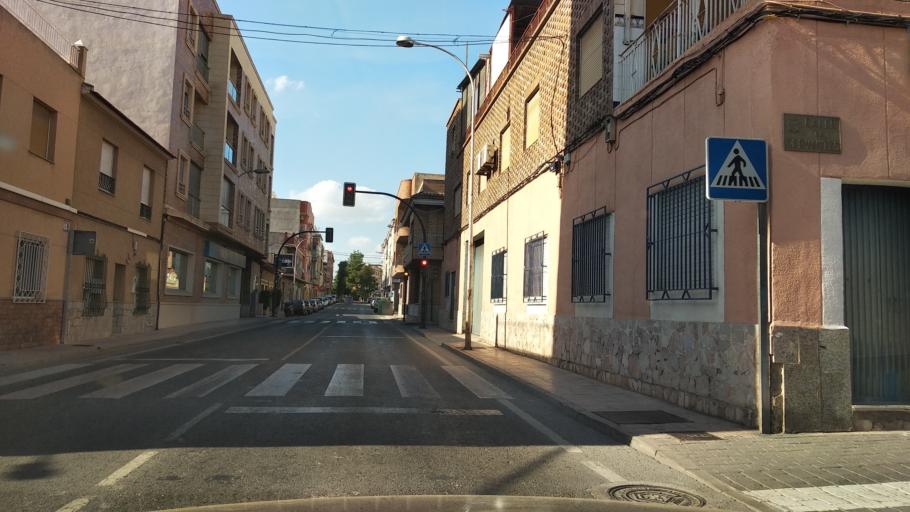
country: ES
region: Murcia
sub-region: Murcia
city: Santomera
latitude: 38.0601
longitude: -1.0523
